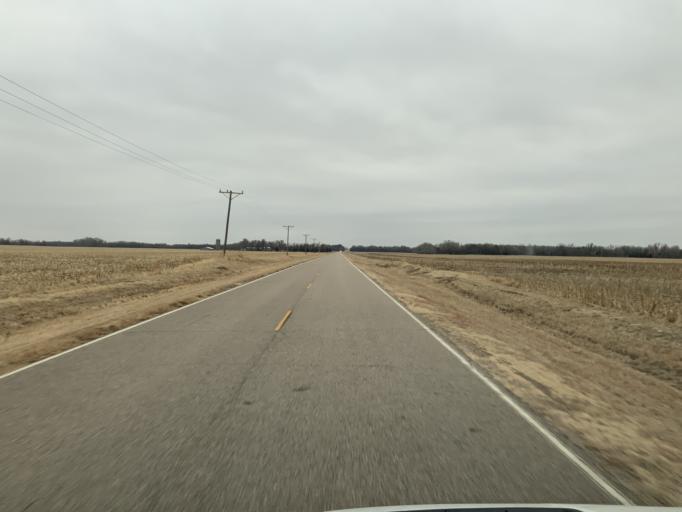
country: US
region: Kansas
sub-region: Reno County
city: South Hutchinson
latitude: 37.9493
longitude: -98.0873
